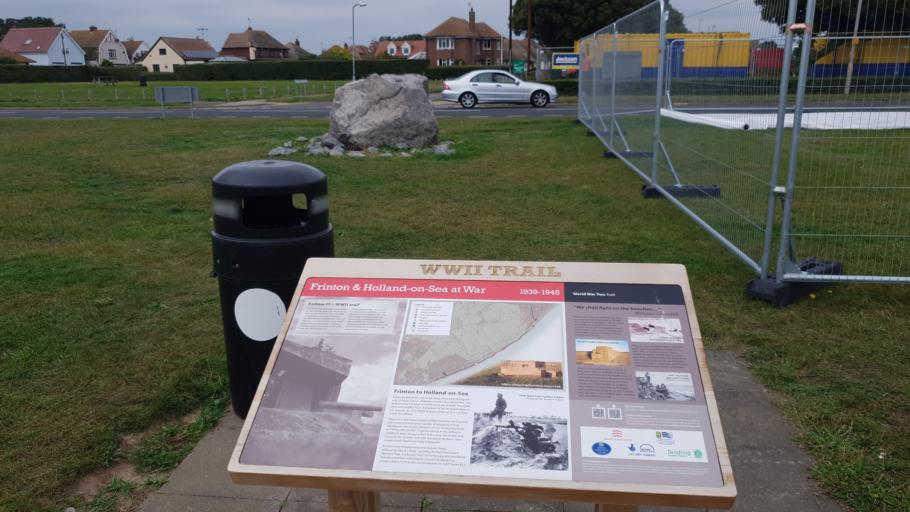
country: GB
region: England
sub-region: Essex
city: Clacton-on-Sea
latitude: 51.7966
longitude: 1.1804
